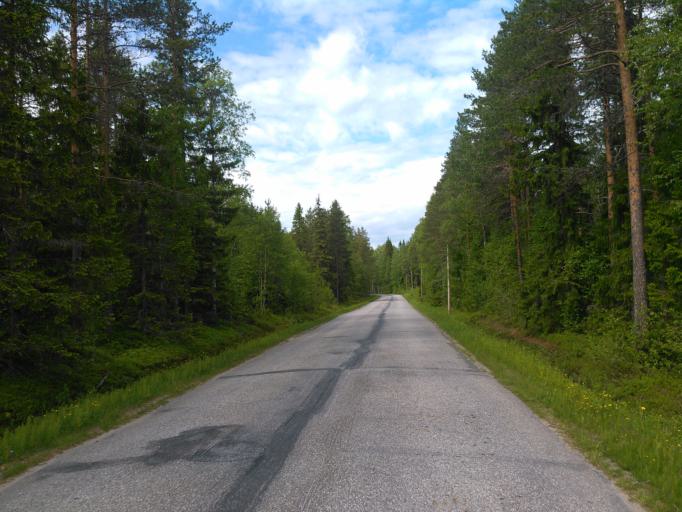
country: SE
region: Vaesterbotten
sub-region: Umea Kommun
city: Ersmark
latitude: 63.8745
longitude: 20.3269
